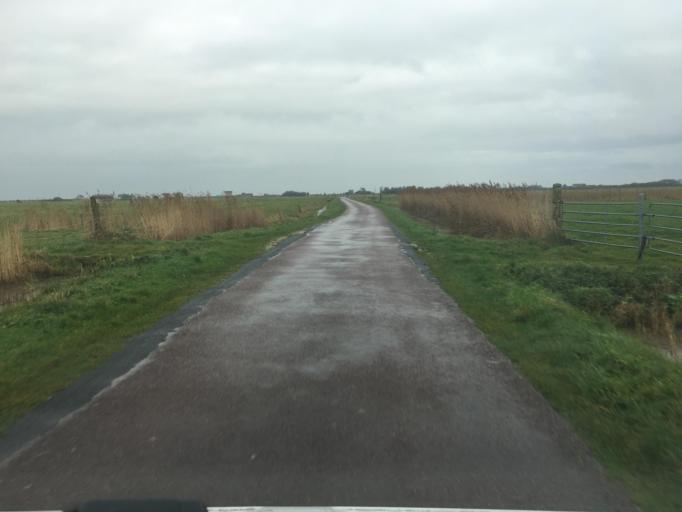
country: FR
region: Lower Normandy
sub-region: Departement de la Manche
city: Sainte-Mere-Eglise
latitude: 49.4486
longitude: -1.2323
